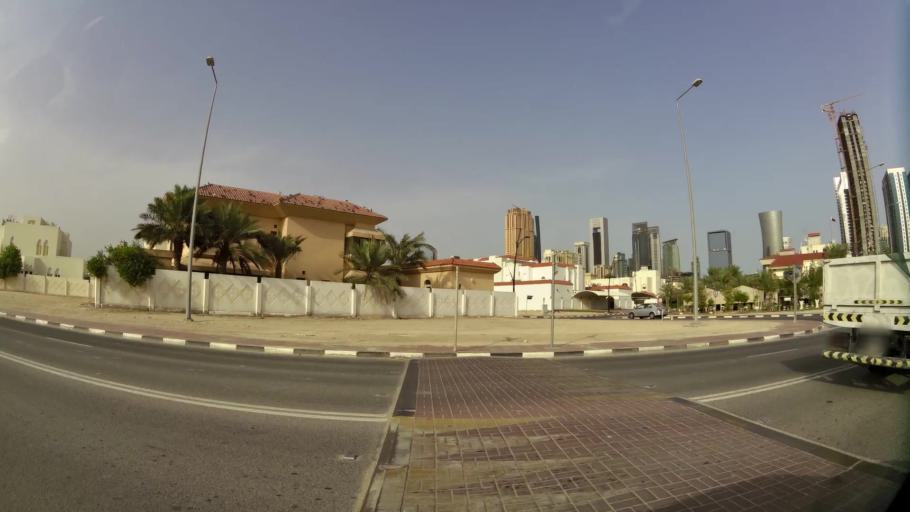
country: QA
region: Baladiyat ad Dawhah
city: Doha
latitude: 25.3205
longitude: 51.5162
